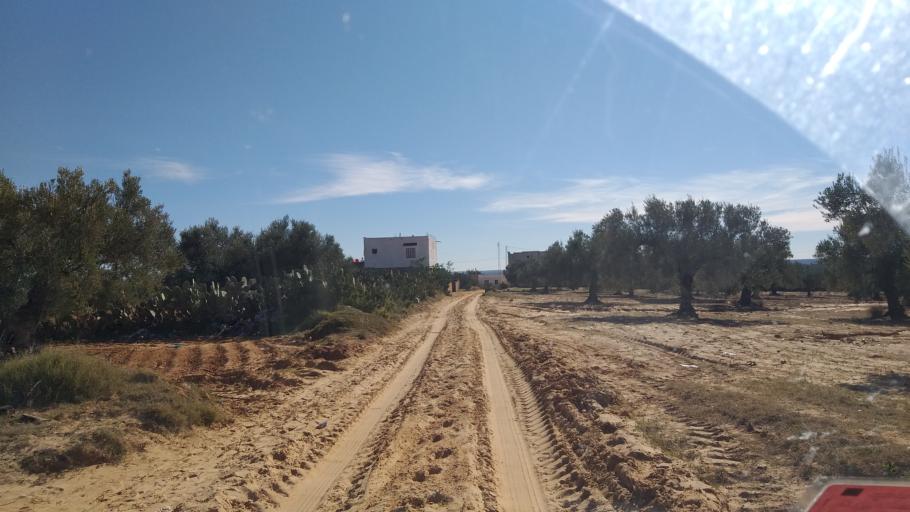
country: TN
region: Al Mahdiyah
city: El Jem
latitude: 35.2556
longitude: 10.6066
